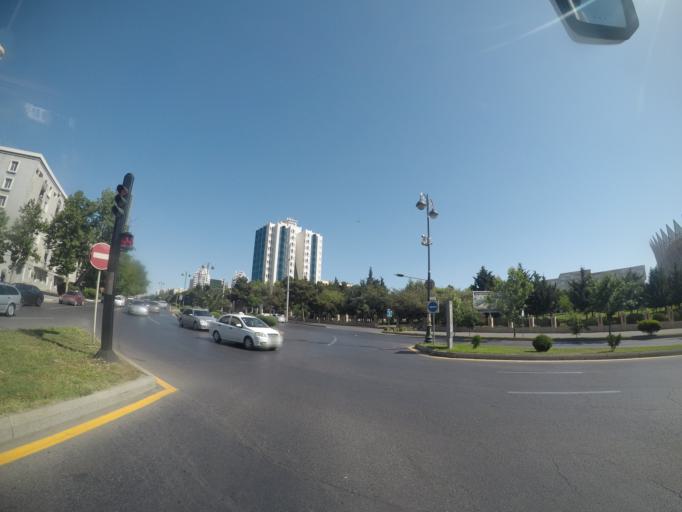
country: AZ
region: Baki
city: Badamdar
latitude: 40.3914
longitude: 49.8228
